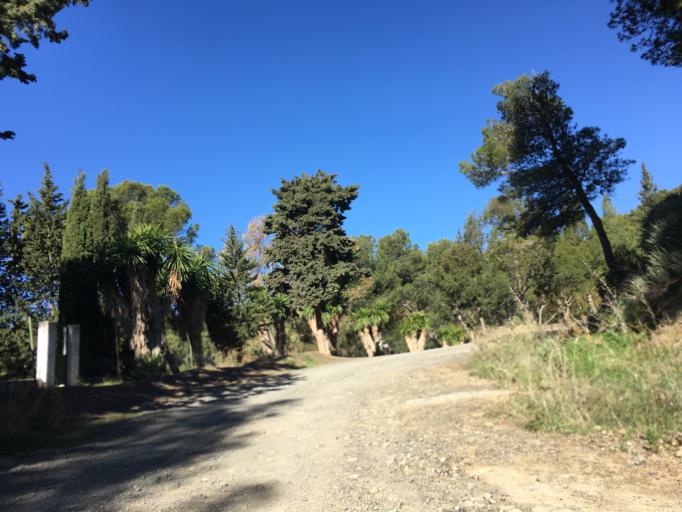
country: ES
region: Andalusia
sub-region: Provincia de Malaga
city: Malaga
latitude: 36.7775
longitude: -4.3851
